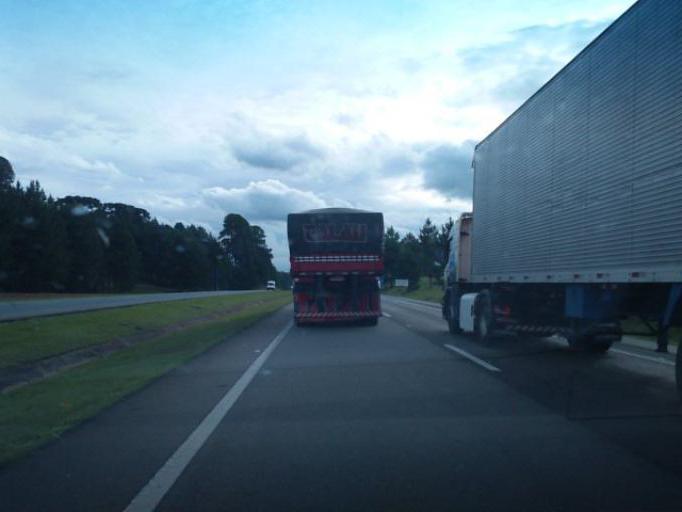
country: BR
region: Parana
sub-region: Piraquara
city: Piraquara
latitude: -25.4176
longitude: -49.0696
